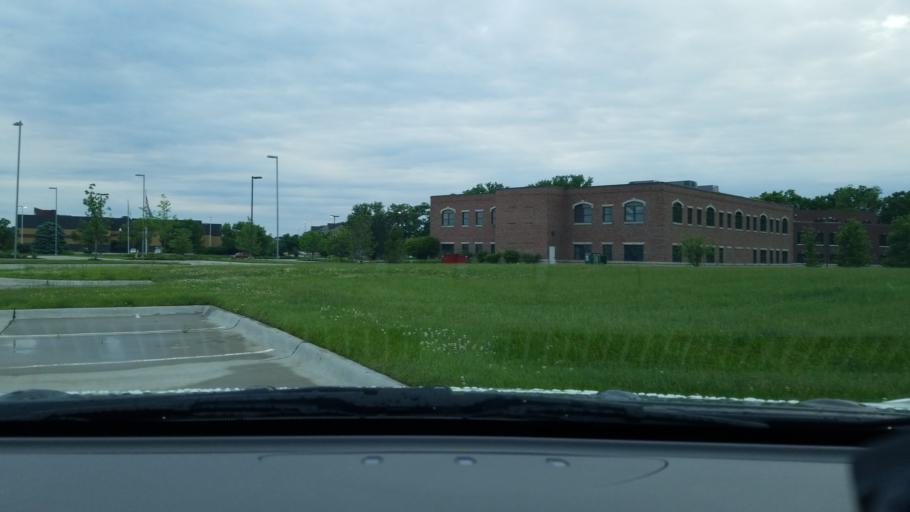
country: US
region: Nebraska
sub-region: Sarpy County
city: Offutt Air Force Base
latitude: 41.1493
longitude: -95.9701
